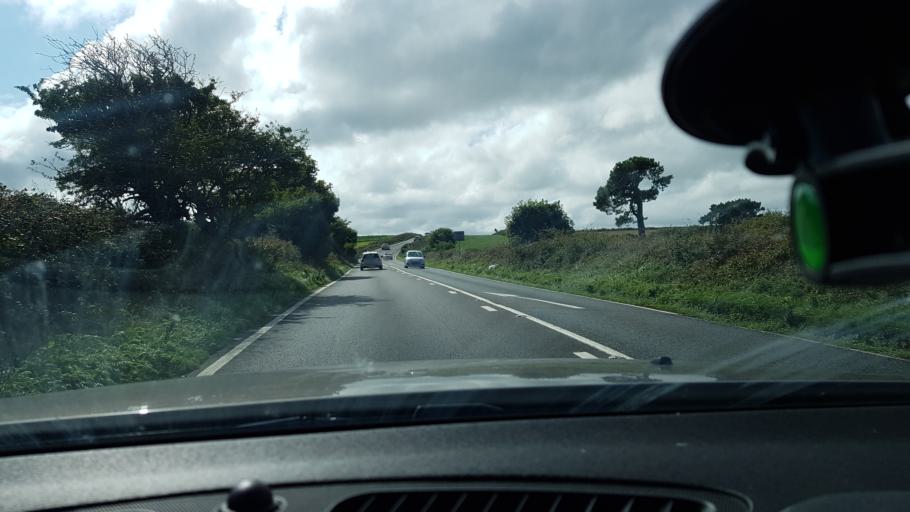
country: GB
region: England
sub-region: Cornwall
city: Perranporth
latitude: 50.3029
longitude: -5.1075
